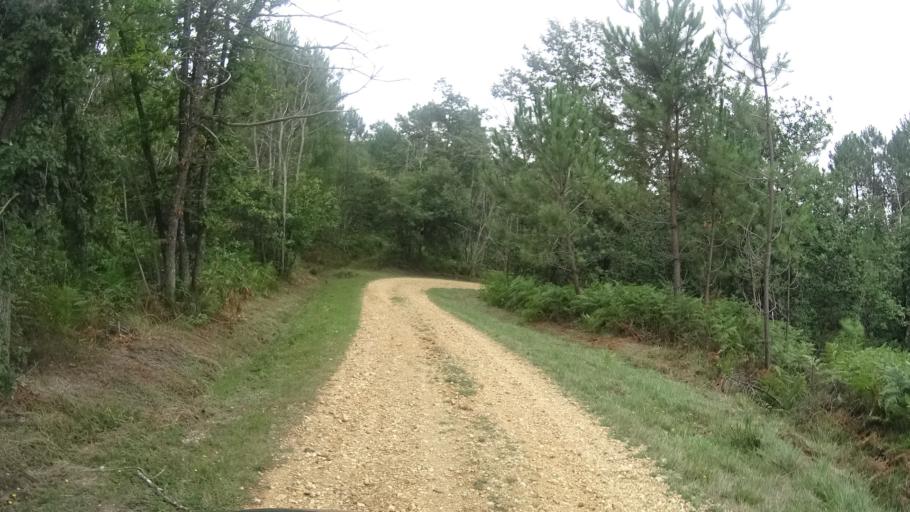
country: FR
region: Aquitaine
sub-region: Departement de la Dordogne
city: Sourzac
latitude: 45.0319
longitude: 0.4152
